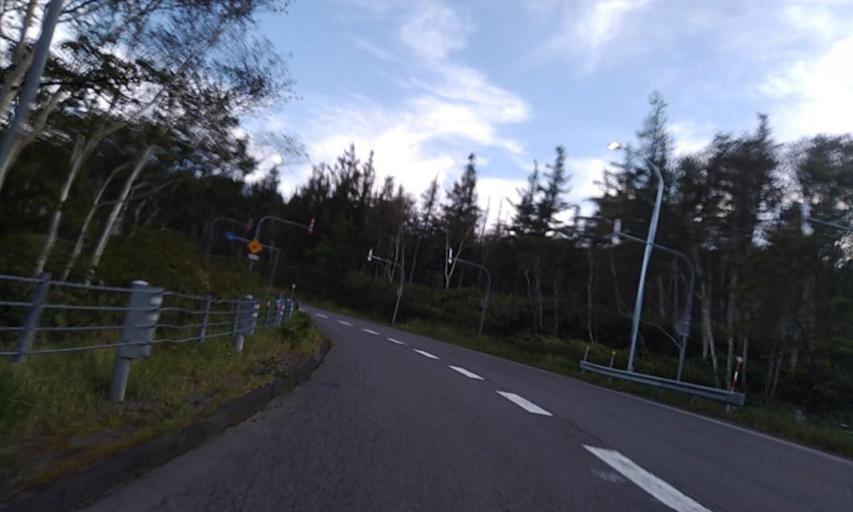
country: JP
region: Hokkaido
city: Otofuke
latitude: 42.9599
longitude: 142.7924
